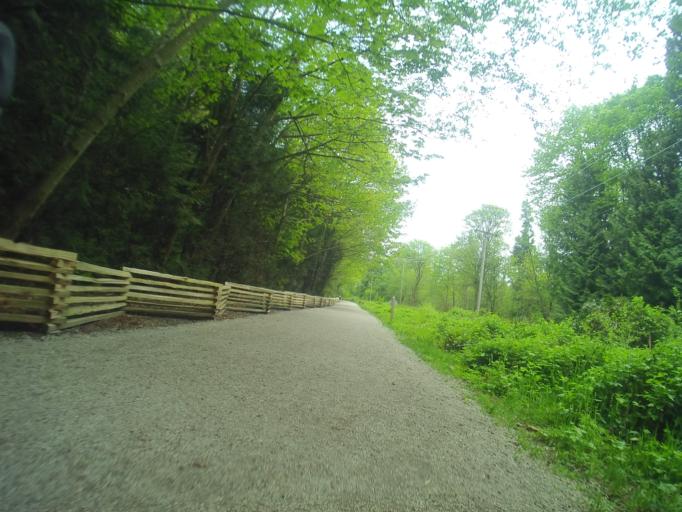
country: CA
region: British Columbia
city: West End
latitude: 49.2488
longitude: -123.2089
